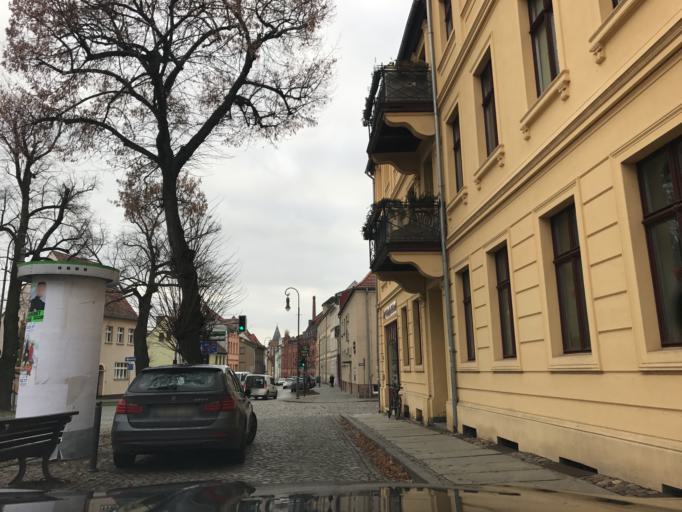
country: DE
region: Brandenburg
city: Brandenburg an der Havel
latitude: 52.4139
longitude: 12.5660
